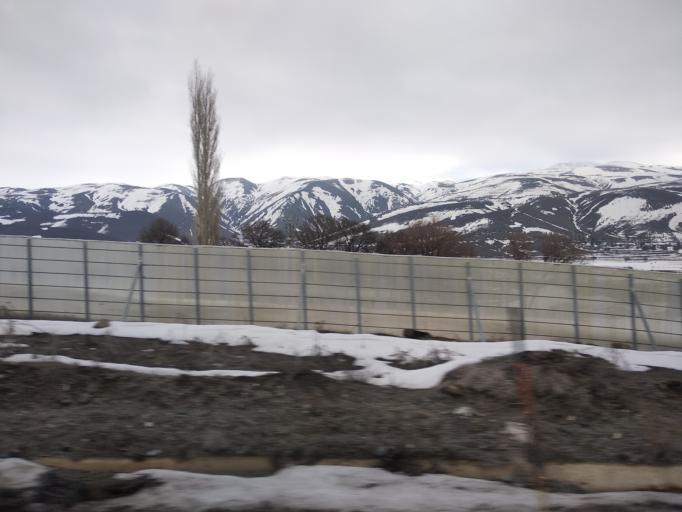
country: TR
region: Erzincan
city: Catalarmut
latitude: 39.8249
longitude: 39.3958
